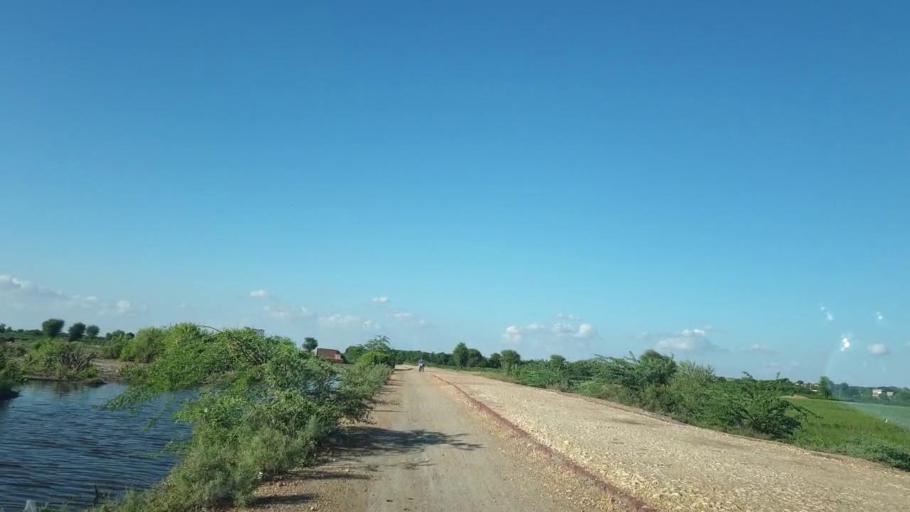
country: PK
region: Sindh
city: Dhoro Naro
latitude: 25.6415
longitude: 69.4983
